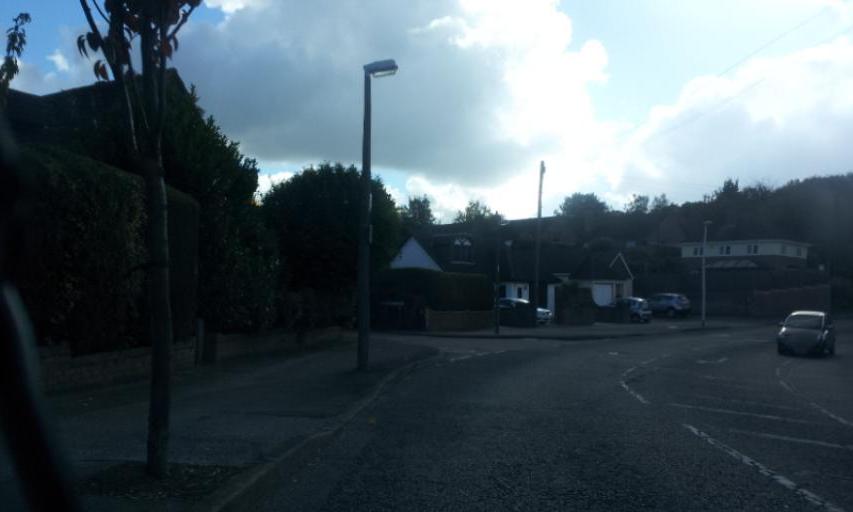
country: GB
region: England
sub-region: Kent
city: Rainham
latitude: 51.3515
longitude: 0.5807
